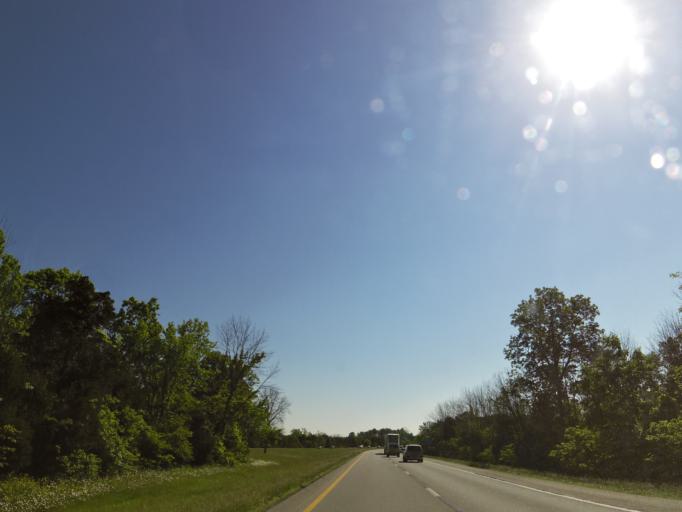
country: US
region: Kentucky
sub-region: Franklin County
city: Frankfort
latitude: 38.1539
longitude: -84.9339
